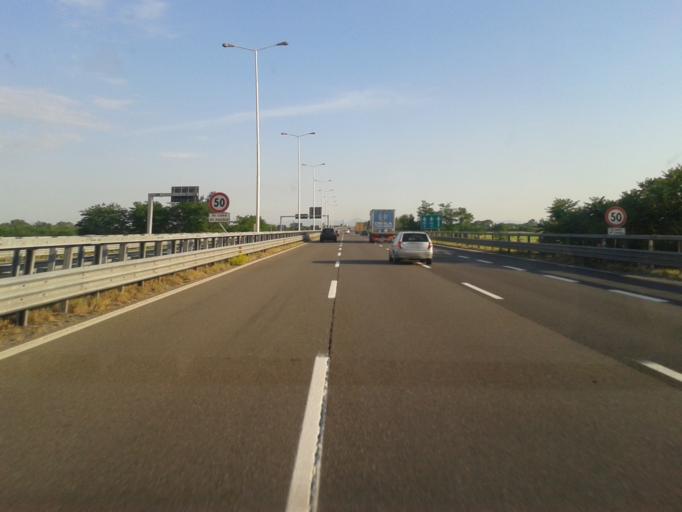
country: IT
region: Piedmont
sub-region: Provincia di Alessandria
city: Tortona
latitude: 44.9072
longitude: 8.8435
